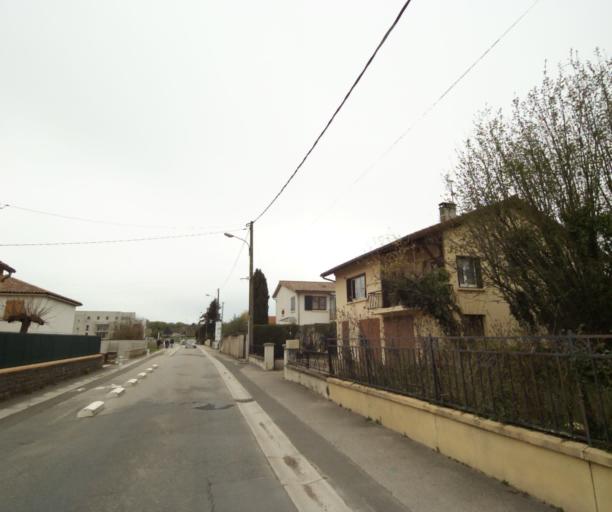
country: FR
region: Bourgogne
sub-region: Departement de Saone-et-Loire
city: Charnay-les-Macon
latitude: 46.3119
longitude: 4.8078
